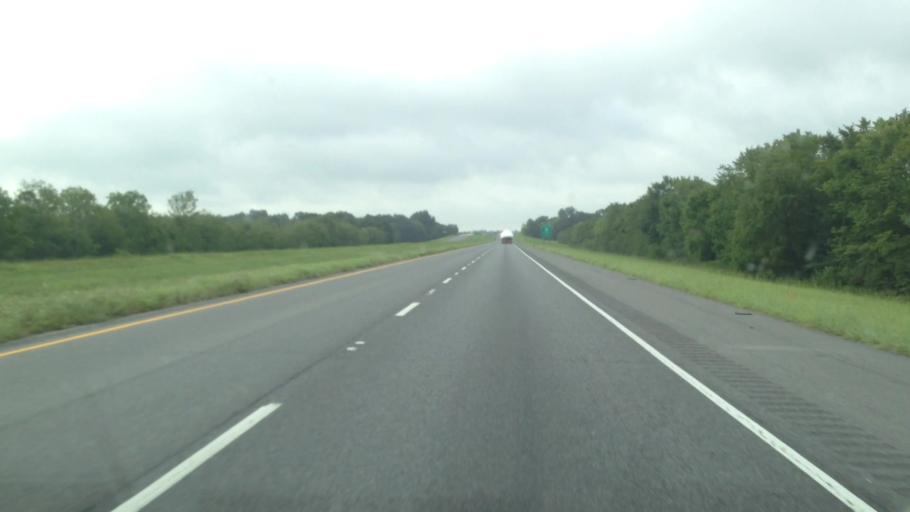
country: US
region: Louisiana
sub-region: Saint Landry Parish
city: Opelousas
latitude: 30.6593
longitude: -92.0648
